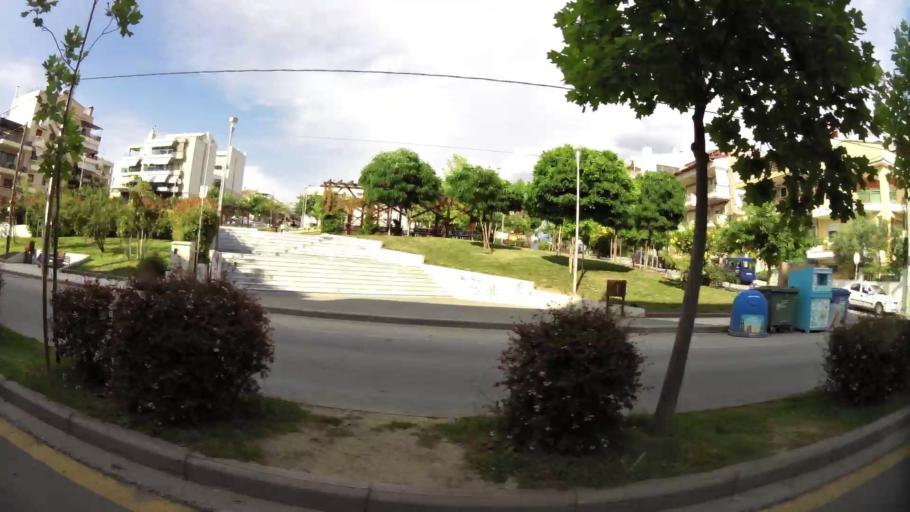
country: GR
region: Central Macedonia
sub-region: Nomos Thessalonikis
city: Kalamaria
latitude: 40.5728
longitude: 22.9659
